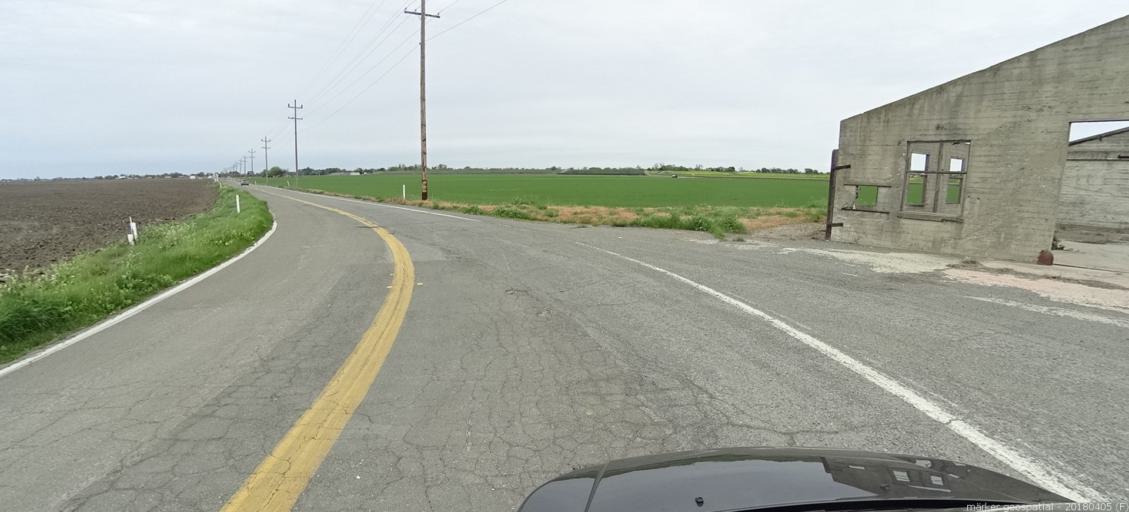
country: US
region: California
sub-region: Sacramento County
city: Walnut Grove
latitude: 38.2844
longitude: -121.5176
